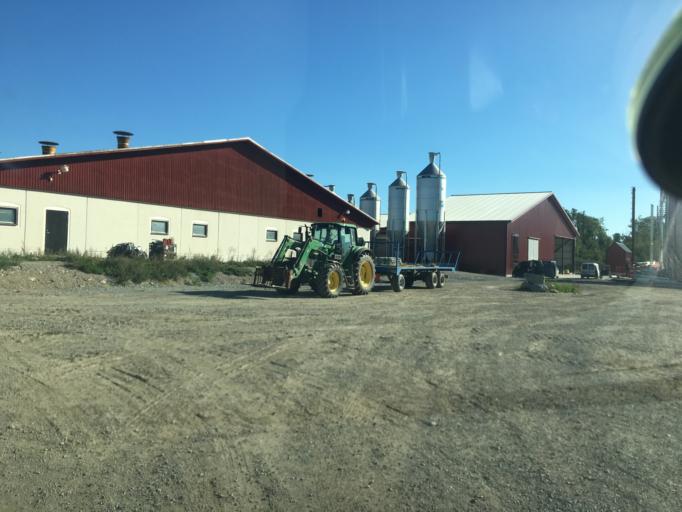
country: SE
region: Vaestmanland
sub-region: Vasteras
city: Tillberga
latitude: 59.7420
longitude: 16.6970
